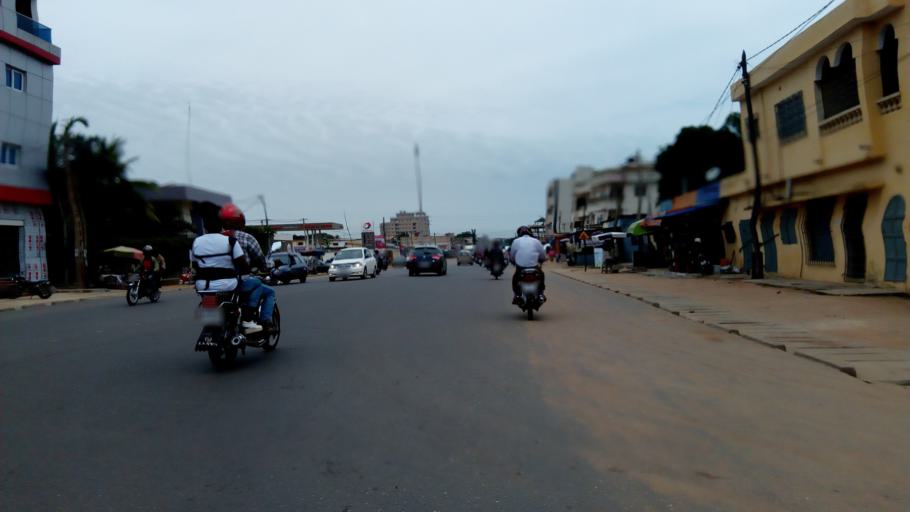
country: TG
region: Maritime
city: Lome
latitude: 6.1537
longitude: 1.2327
